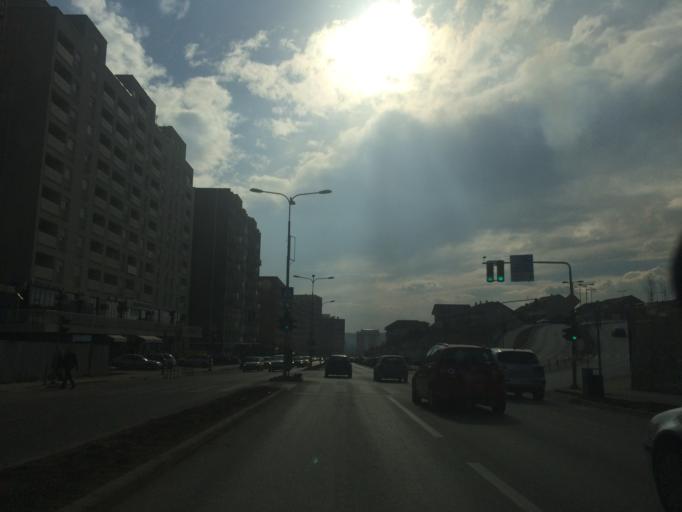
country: XK
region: Pristina
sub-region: Komuna e Prishtines
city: Pristina
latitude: 42.6493
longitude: 21.1730
